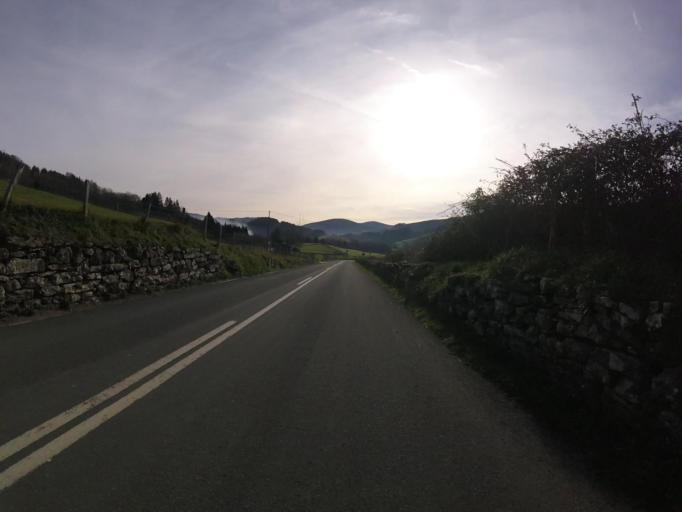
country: ES
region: Basque Country
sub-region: Provincia de Guipuzcoa
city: Berastegui
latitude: 43.1145
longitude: -1.9657
